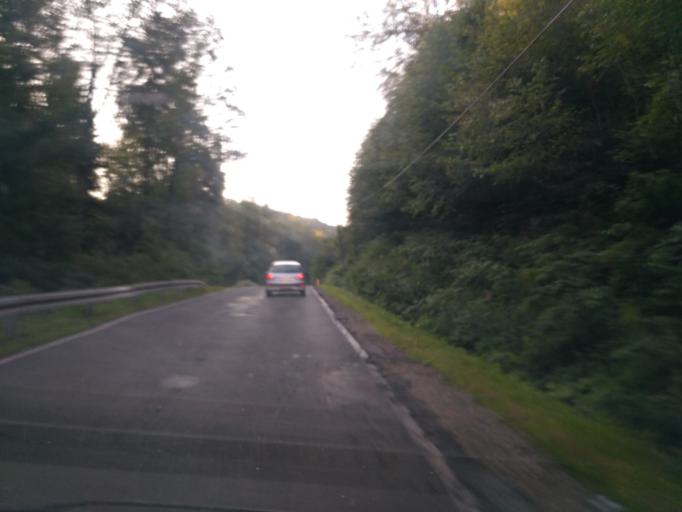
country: PL
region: Subcarpathian Voivodeship
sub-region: Powiat krosnienski
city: Korczyna
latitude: 49.7551
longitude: 21.7964
